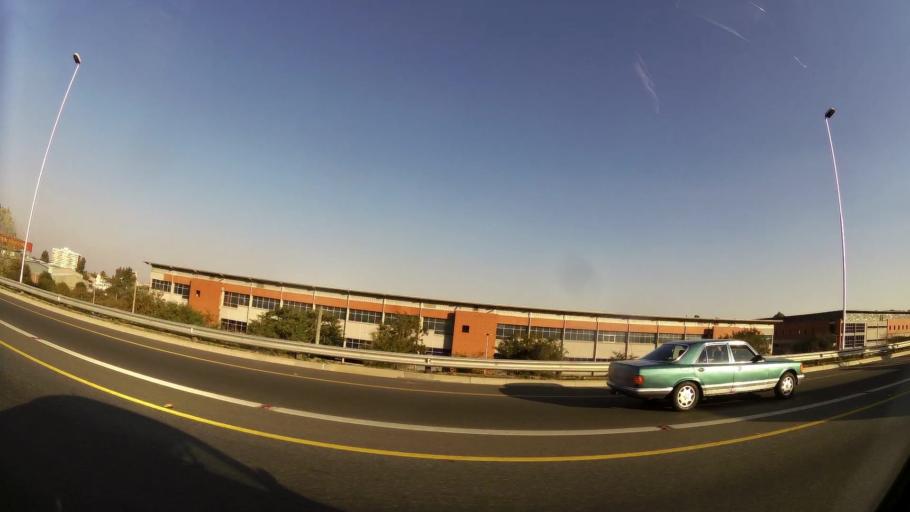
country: ZA
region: Gauteng
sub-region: Ekurhuleni Metropolitan Municipality
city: Germiston
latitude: -26.2592
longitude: 28.1140
